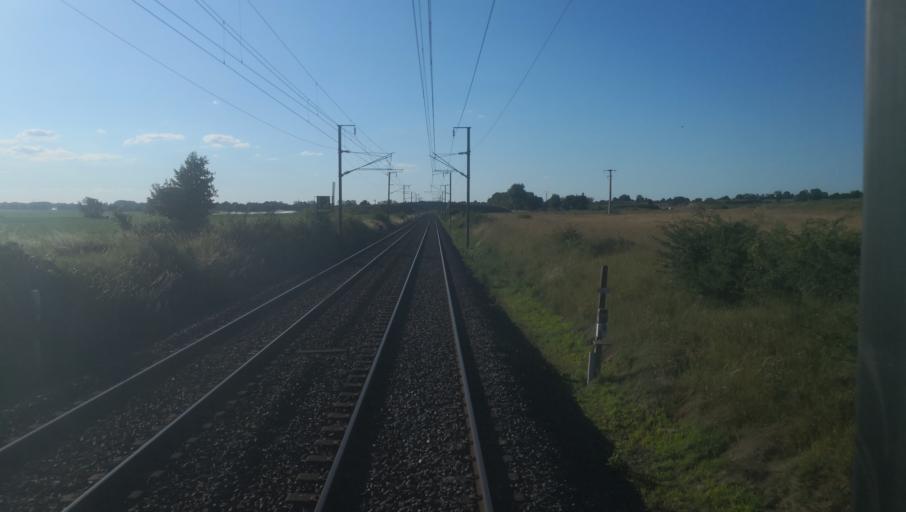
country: FR
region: Auvergne
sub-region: Departement de l'Allier
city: Trevol
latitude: 46.6407
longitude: 3.2733
